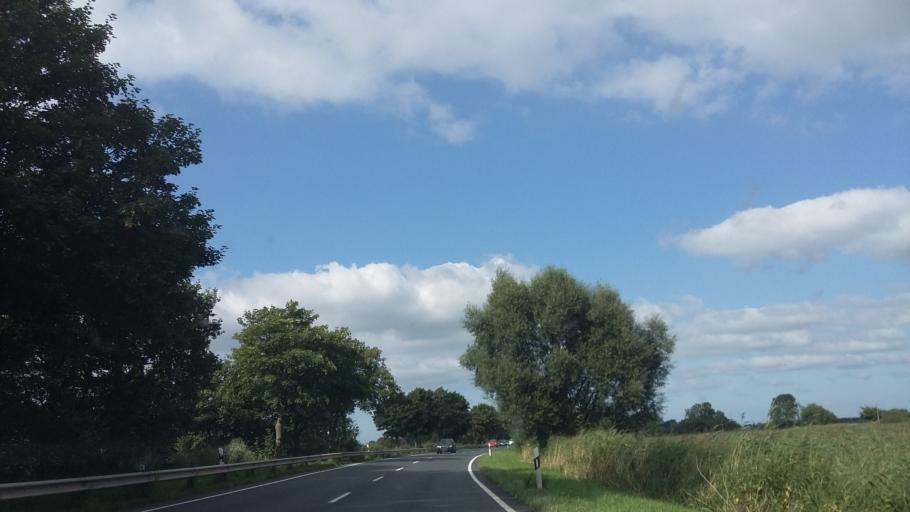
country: DE
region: Lower Saxony
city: Loxstedt
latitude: 53.4720
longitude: 8.5971
